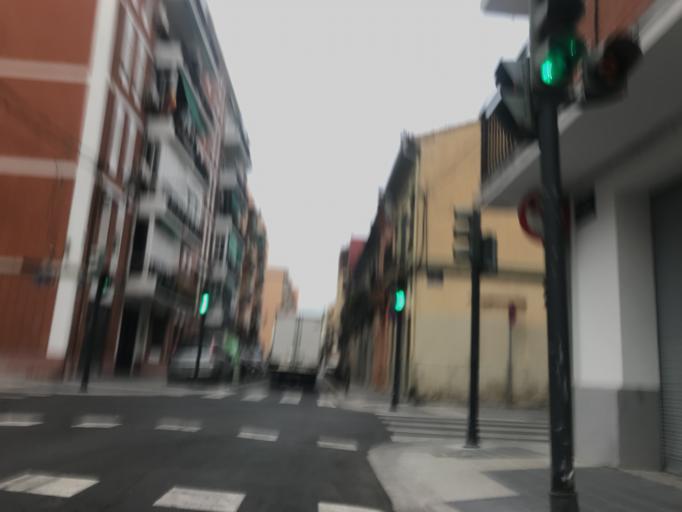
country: ES
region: Valencia
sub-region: Provincia de Valencia
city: Valencia
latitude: 39.4660
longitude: -0.3442
